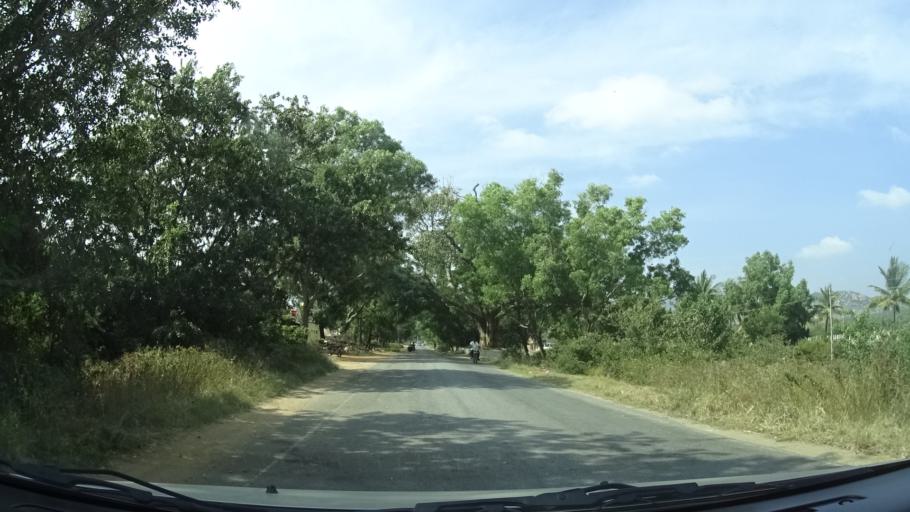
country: IN
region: Karnataka
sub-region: Chikkaballapur
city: Chik Ballapur
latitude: 13.4050
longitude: 77.7108
